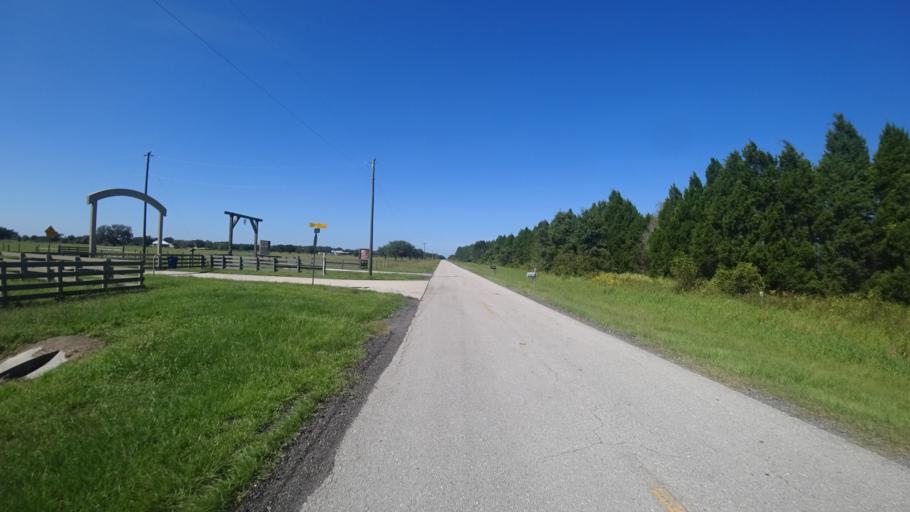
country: US
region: Florida
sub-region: Sarasota County
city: Warm Mineral Springs
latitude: 27.2736
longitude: -82.1462
